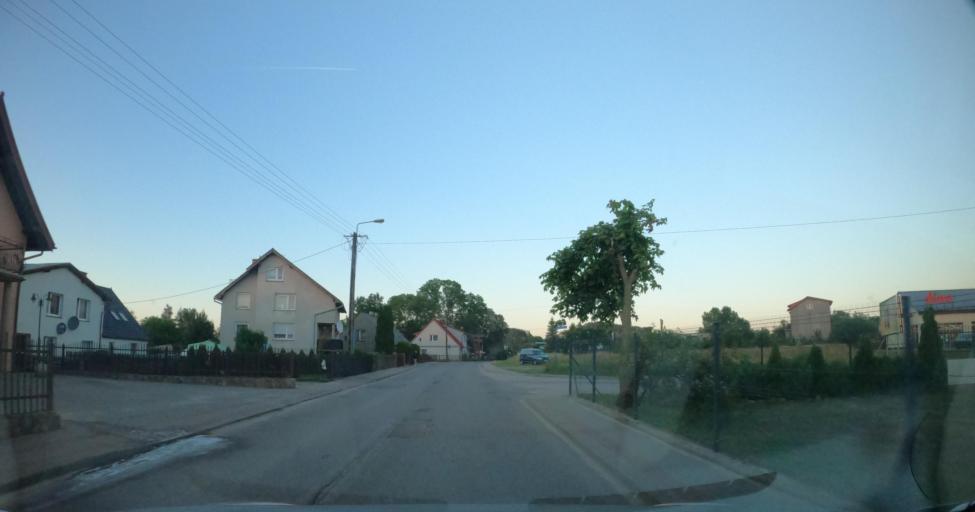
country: PL
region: Pomeranian Voivodeship
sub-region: Powiat wejherowski
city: Linia
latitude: 54.4512
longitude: 17.9302
